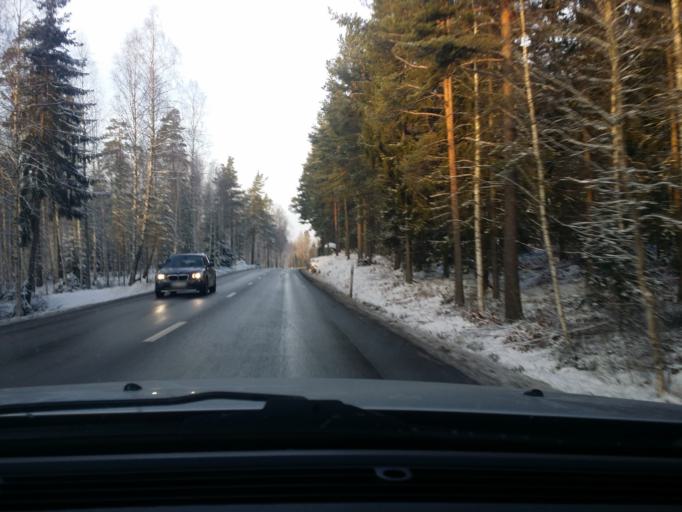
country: SE
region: OErebro
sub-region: Lindesbergs Kommun
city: Frovi
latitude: 59.5113
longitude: 15.3507
